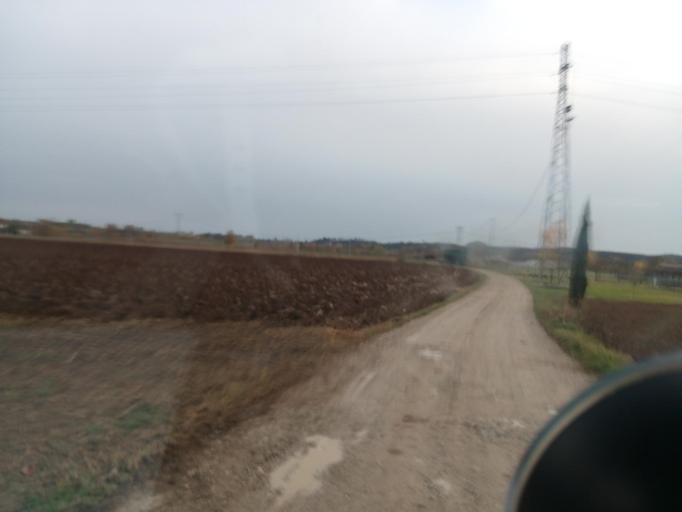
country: IT
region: Lombardy
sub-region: Provincia di Brescia
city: Pozzolengo
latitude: 45.3942
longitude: 10.6287
